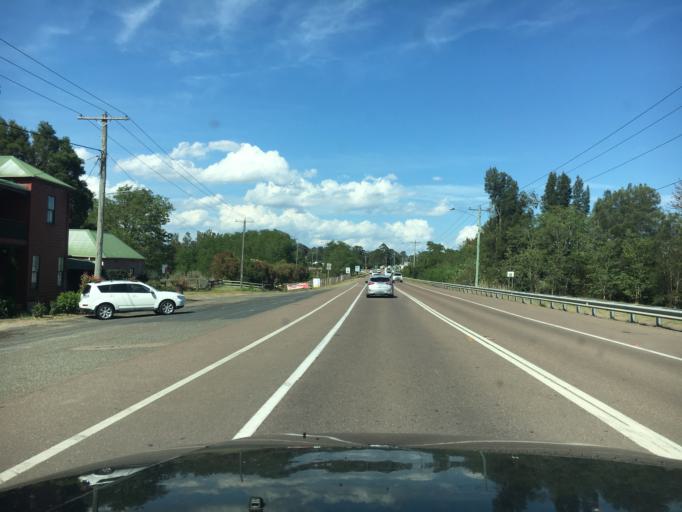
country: AU
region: New South Wales
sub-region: Cessnock
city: Branxton
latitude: -32.6560
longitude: 151.3538
